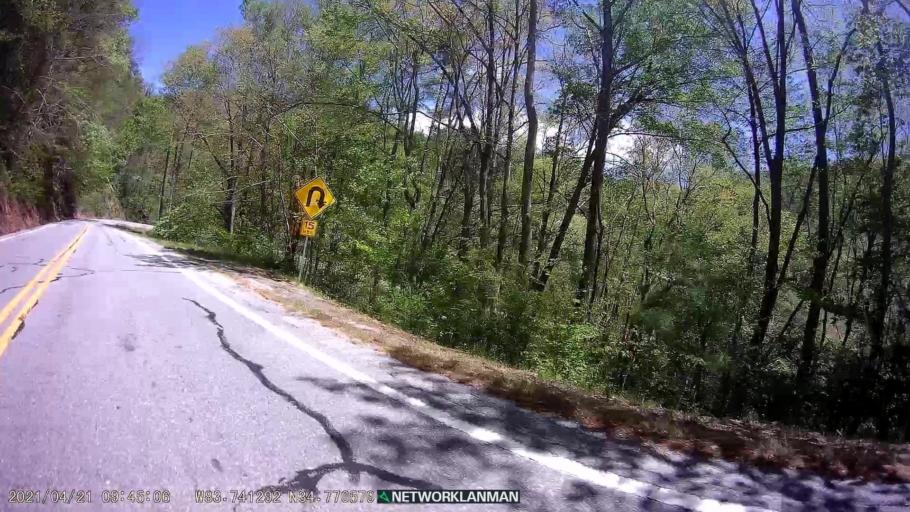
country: US
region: Georgia
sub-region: Towns County
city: Hiawassee
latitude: 34.7766
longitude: -83.7413
